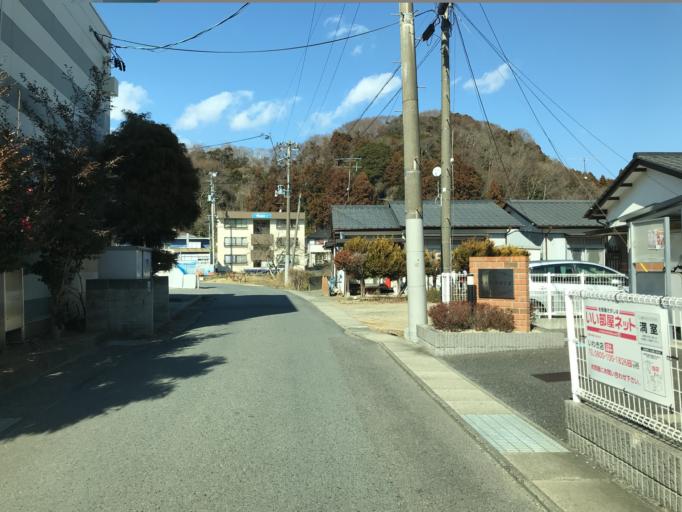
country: JP
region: Fukushima
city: Iwaki
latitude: 37.0378
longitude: 140.8974
